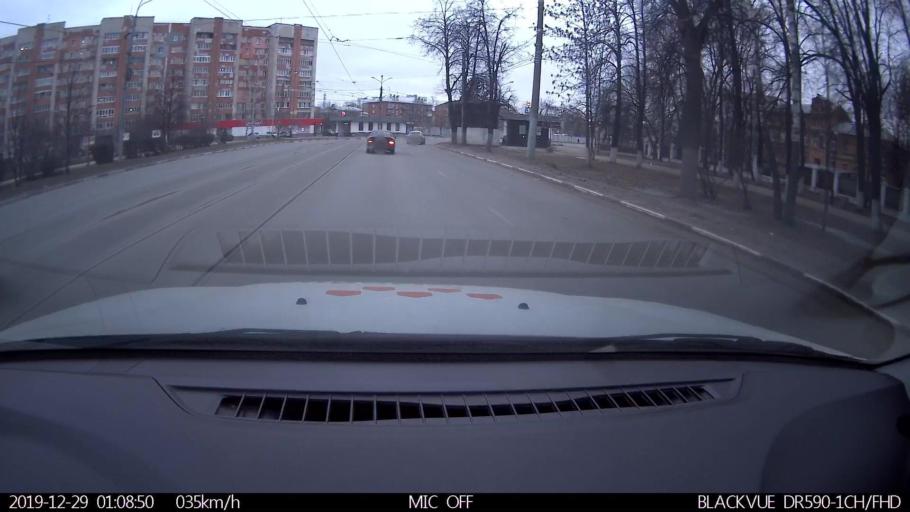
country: RU
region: Nizjnij Novgorod
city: Nizhniy Novgorod
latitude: 56.3121
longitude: 43.9367
